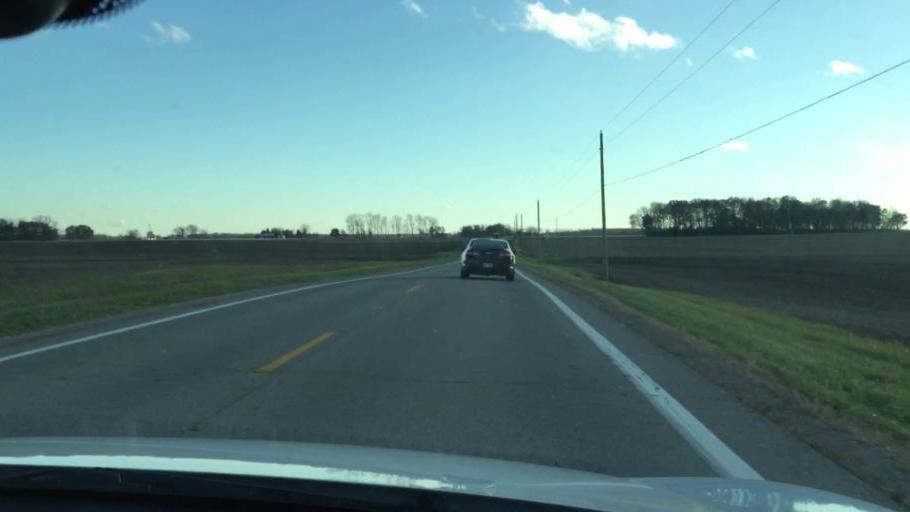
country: US
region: Ohio
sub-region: Champaign County
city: North Lewisburg
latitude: 40.1617
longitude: -83.5270
